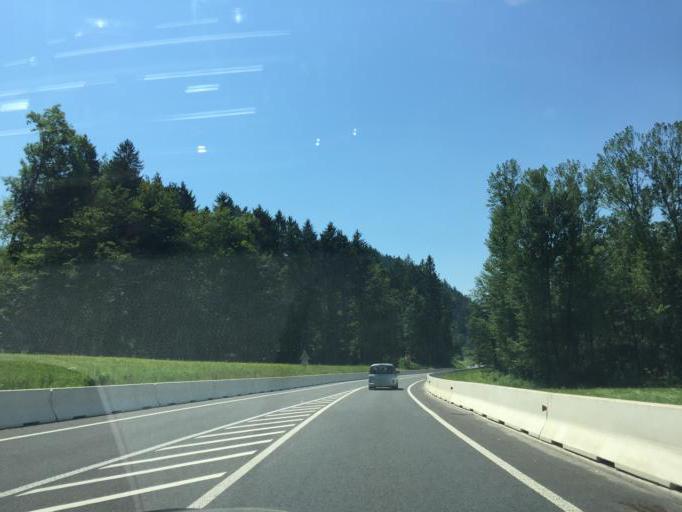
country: SI
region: Skofja Loka
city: Skofja Loka
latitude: 46.1564
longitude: 14.3092
